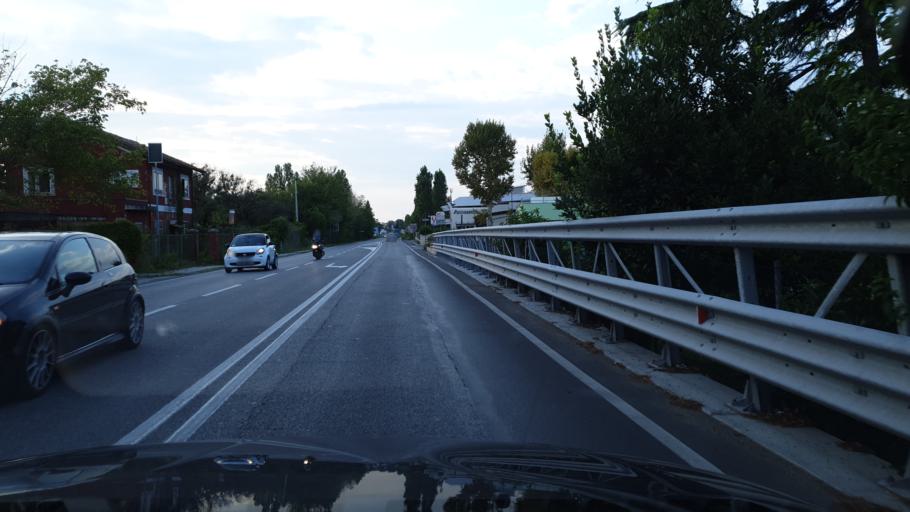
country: IT
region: Emilia-Romagna
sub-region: Provincia di Rimini
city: Rivazzurra
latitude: 44.0268
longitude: 12.6144
